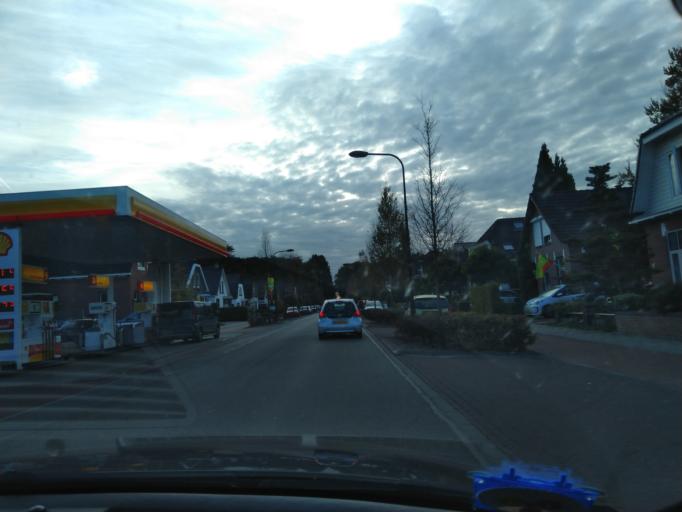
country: NL
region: Drenthe
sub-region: Gemeente Tynaarlo
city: Zuidlaren
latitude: 53.0884
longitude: 6.6635
